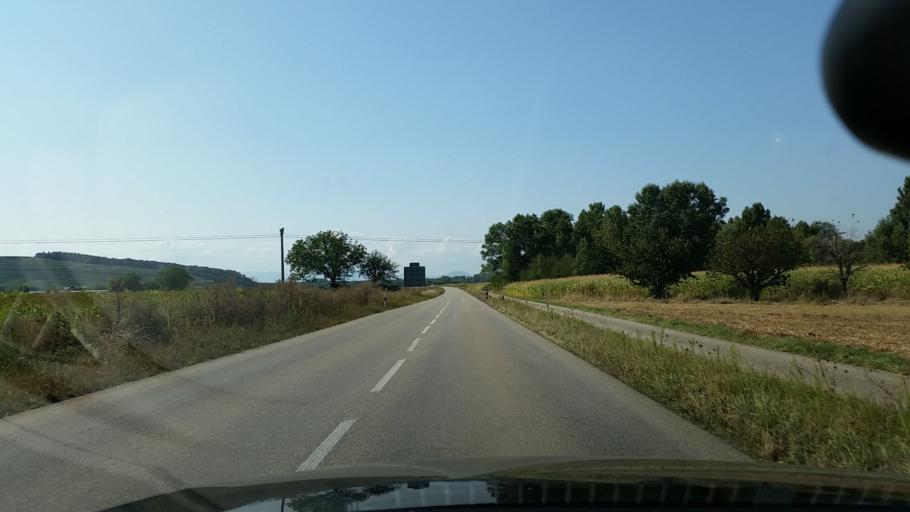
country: DE
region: Baden-Wuerttemberg
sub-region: Freiburg Region
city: Wyhl
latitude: 48.1531
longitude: 7.6325
